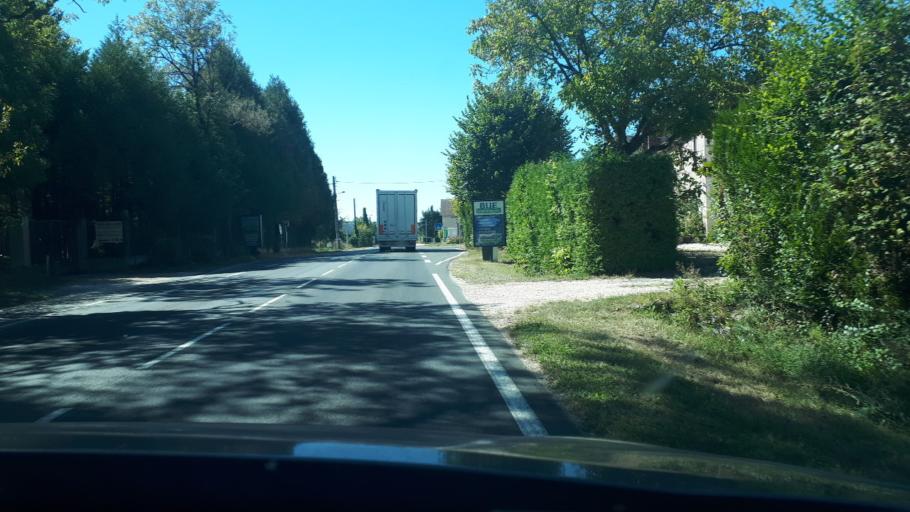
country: FR
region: Centre
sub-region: Departement du Cher
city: Sancerre
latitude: 47.3028
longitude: 2.7967
